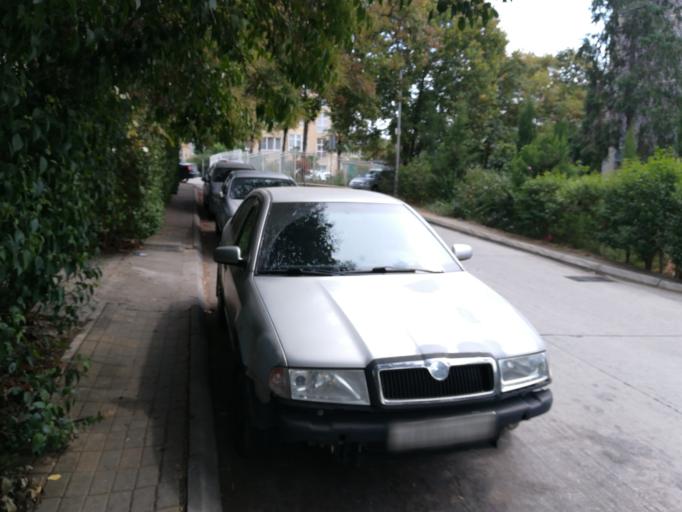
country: RU
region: Krasnodarskiy
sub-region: Sochi City
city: Sochi
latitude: 43.5930
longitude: 39.7338
